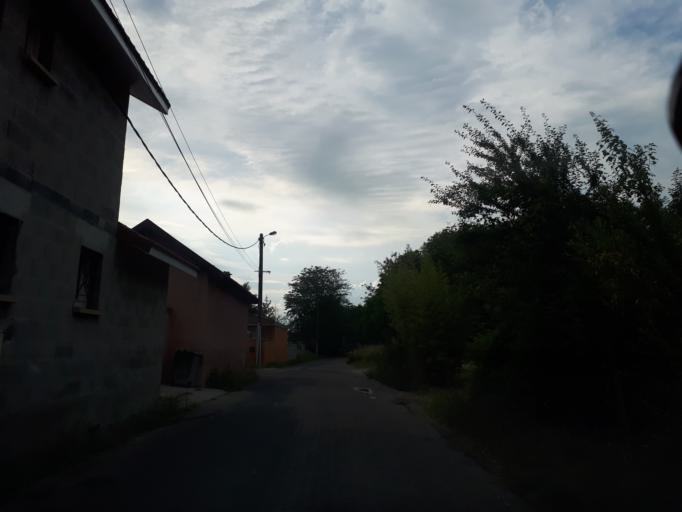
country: FR
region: Rhone-Alpes
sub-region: Departement de l'Isere
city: Bourgoin-Jallieu
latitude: 45.5966
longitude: 5.2781
